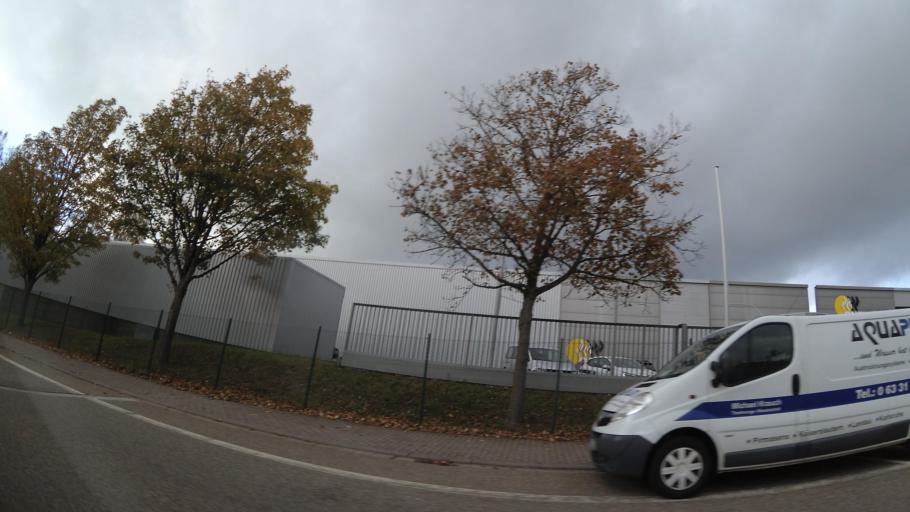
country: DE
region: Rheinland-Pfalz
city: Obersimten
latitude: 49.1843
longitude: 7.5747
